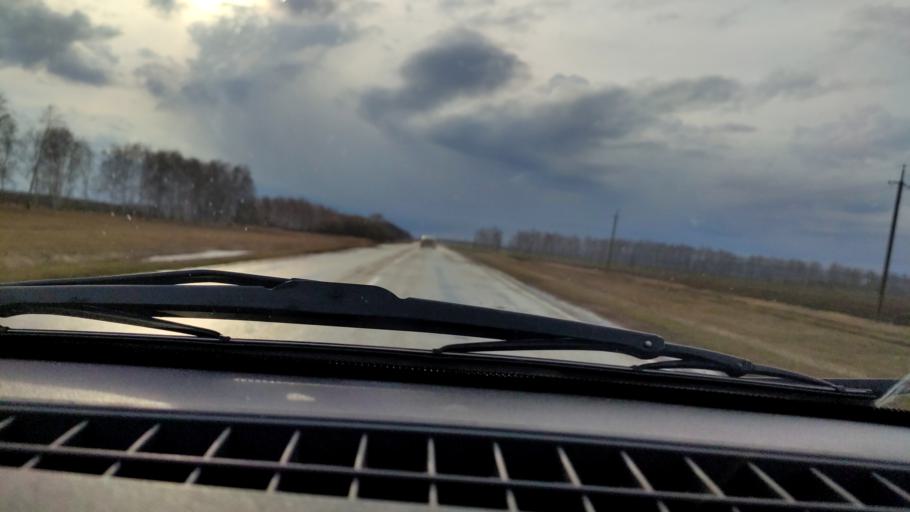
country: RU
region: Bashkortostan
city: Alekseyevka
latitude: 55.1054
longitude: 55.0074
